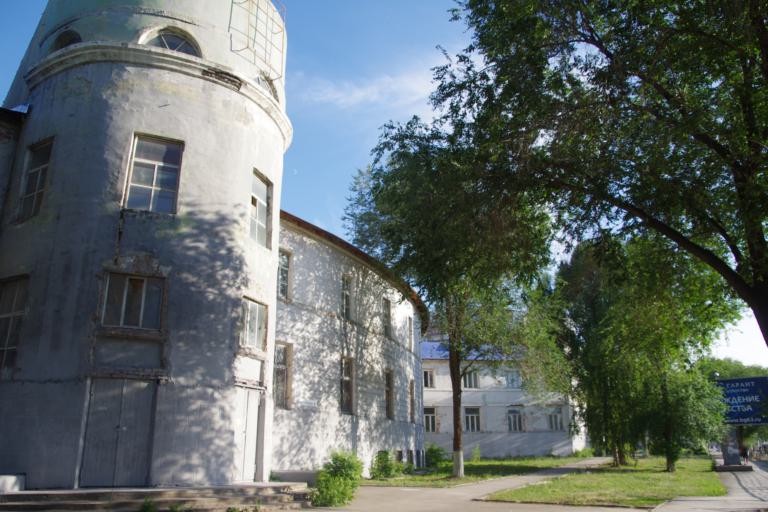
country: RU
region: Samara
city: Samara
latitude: 53.2161
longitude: 50.1486
